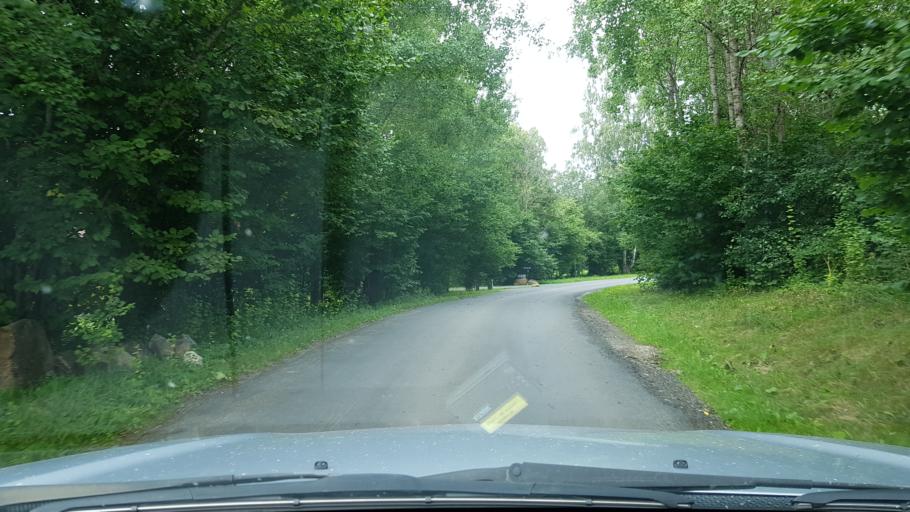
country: EE
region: Harju
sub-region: Rae vald
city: Vaida
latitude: 59.3462
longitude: 24.9601
